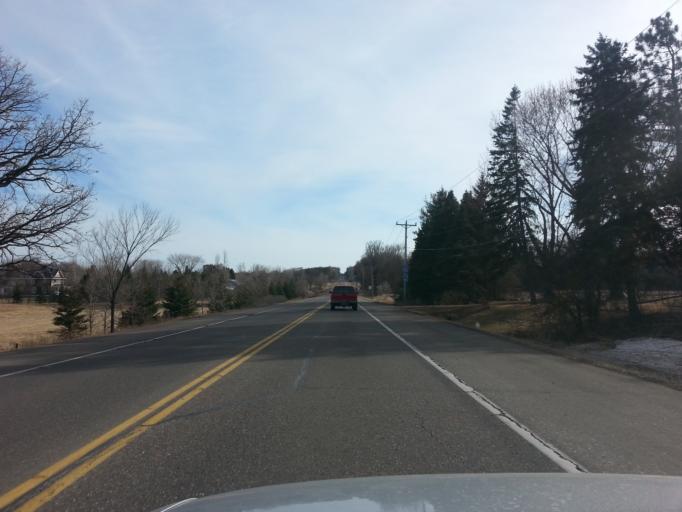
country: US
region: Minnesota
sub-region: Washington County
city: Lake Elmo
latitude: 44.9426
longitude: -92.8627
